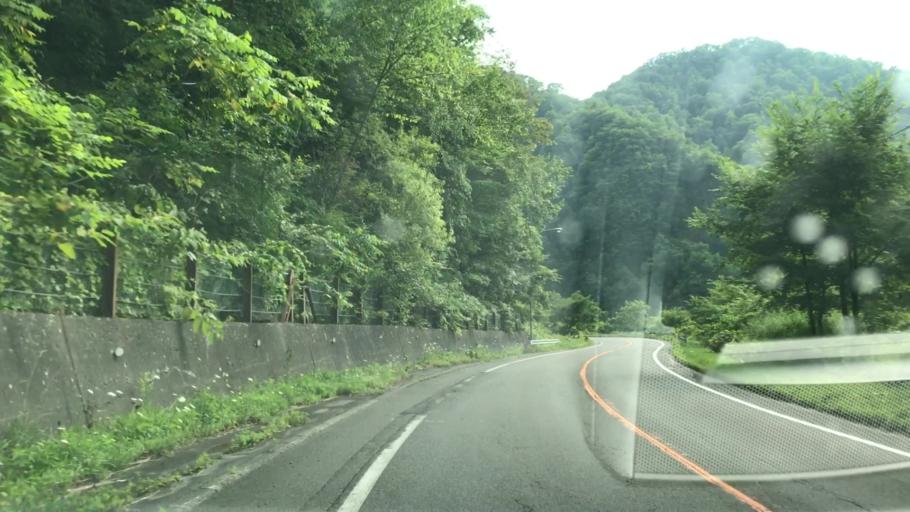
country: JP
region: Hokkaido
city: Shizunai-furukawacho
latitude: 42.7950
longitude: 142.3946
